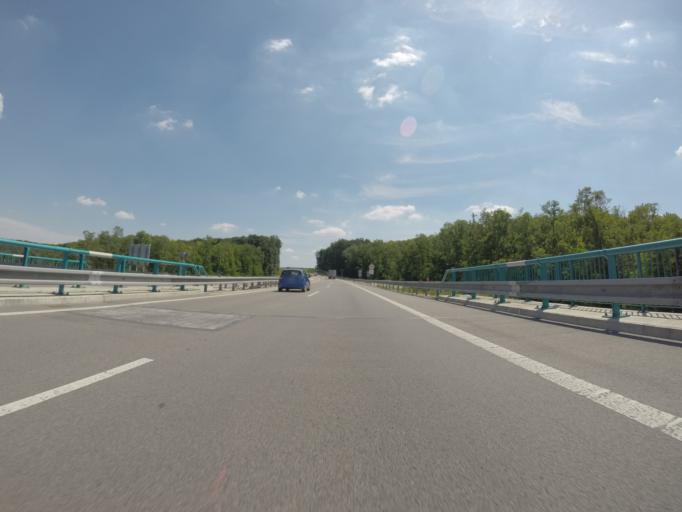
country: SK
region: Nitriansky
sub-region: Okres Nitra
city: Nitra
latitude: 48.3039
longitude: 18.0188
